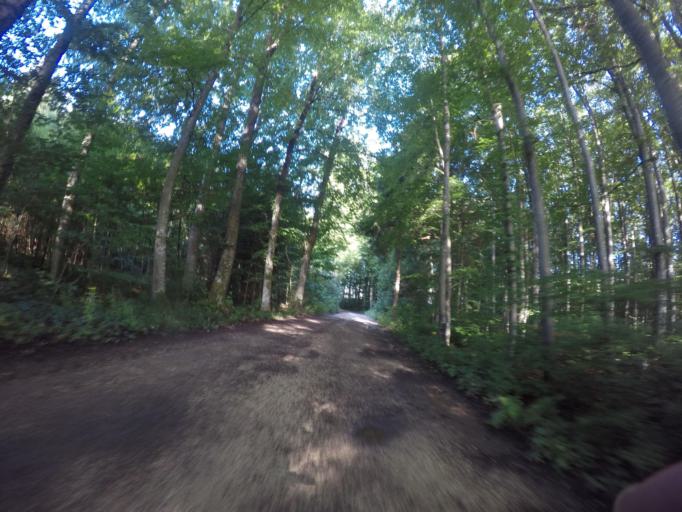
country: DE
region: Baden-Wuerttemberg
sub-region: Tuebingen Region
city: Schelklingen
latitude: 48.3944
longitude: 9.6924
